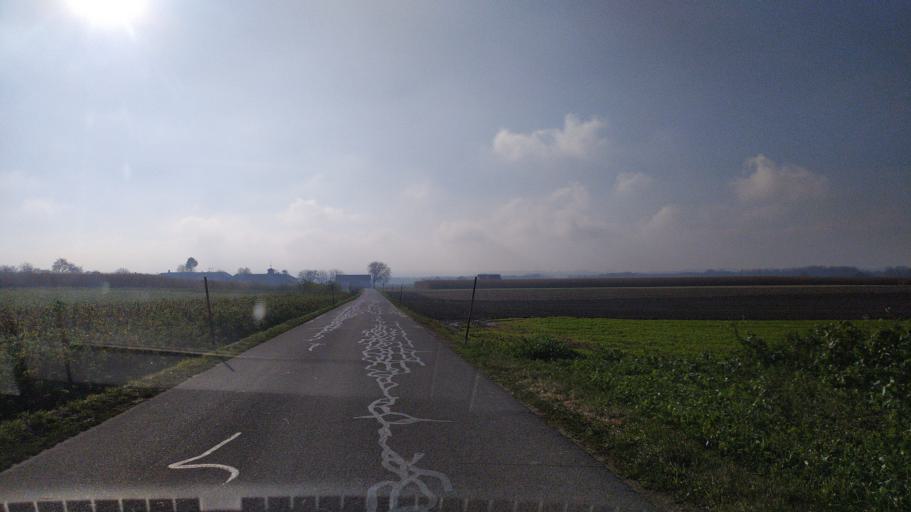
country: AT
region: Upper Austria
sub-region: Politischer Bezirk Perg
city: Perg
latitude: 48.1997
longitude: 14.6517
